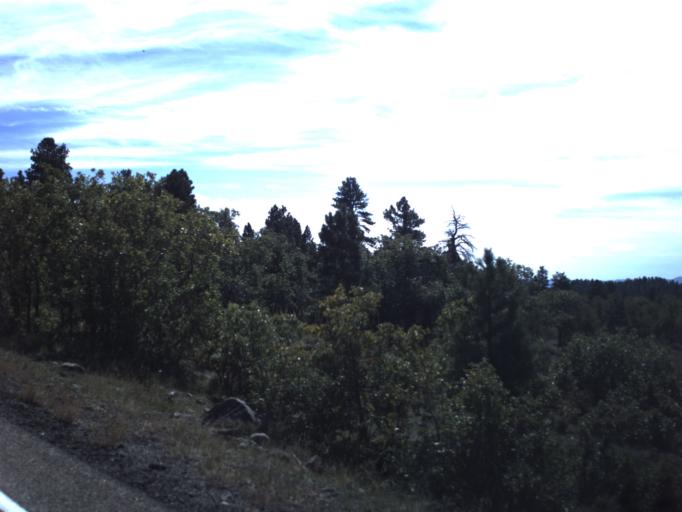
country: US
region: Utah
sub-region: Wayne County
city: Loa
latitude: 38.0079
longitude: -111.3960
